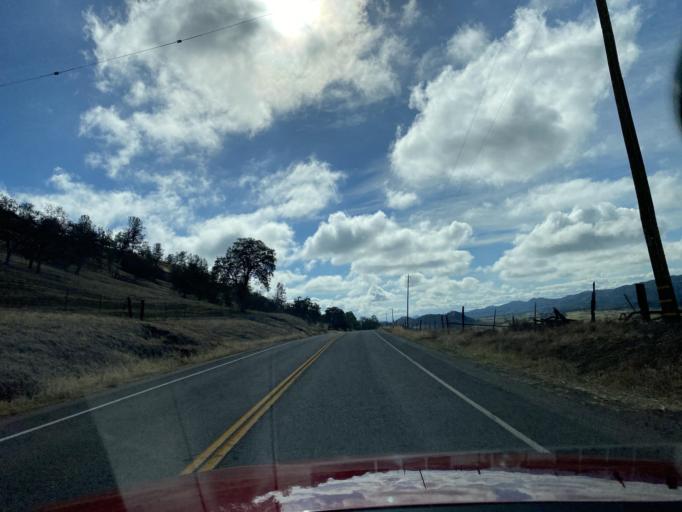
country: US
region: California
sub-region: Glenn County
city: Willows
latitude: 39.5551
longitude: -122.5407
